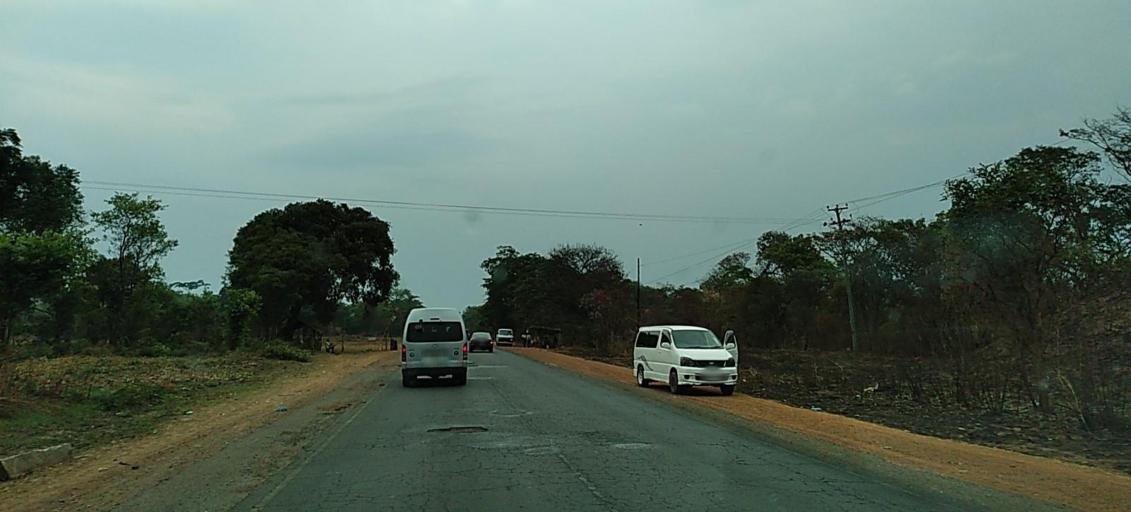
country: ZM
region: Copperbelt
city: Luanshya
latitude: -13.0825
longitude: 28.4433
